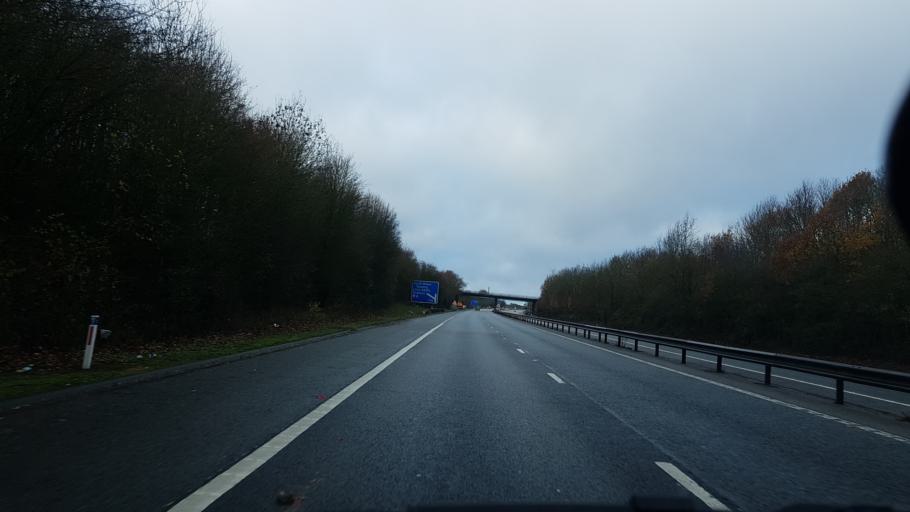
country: GB
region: England
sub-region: Wokingham
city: Wokingham
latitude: 51.4269
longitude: -0.8353
